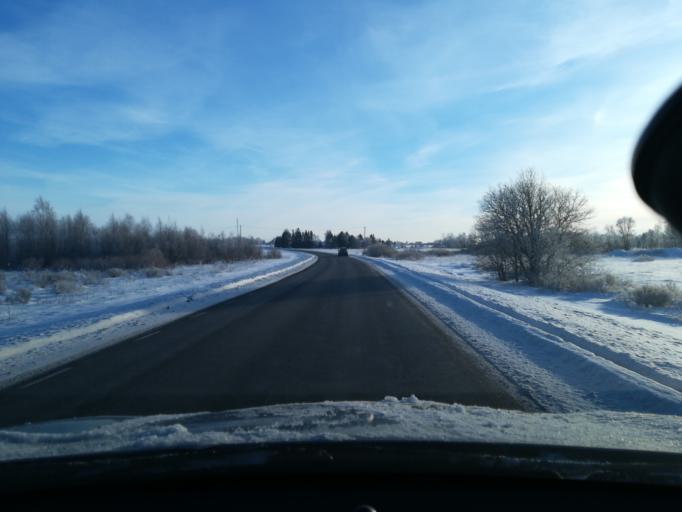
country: EE
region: Harju
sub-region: Harku vald
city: Tabasalu
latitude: 59.3710
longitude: 24.4750
